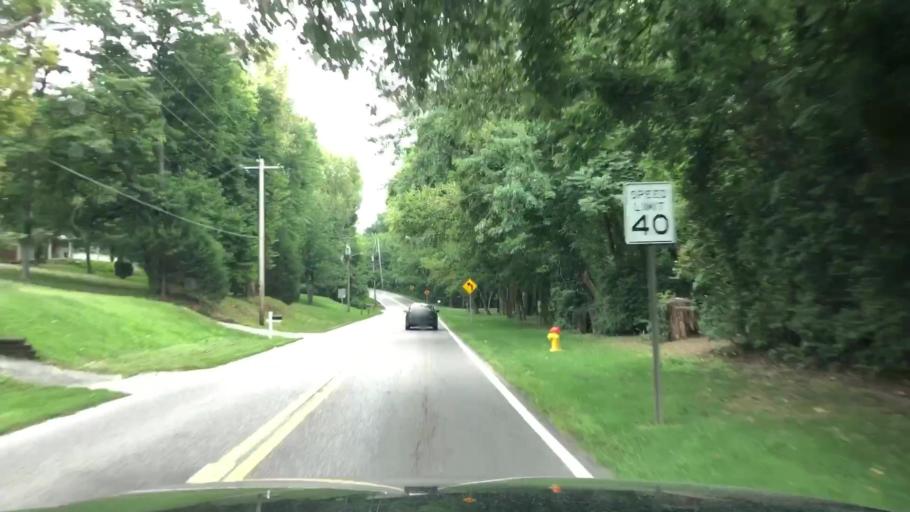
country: US
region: Missouri
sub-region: Saint Louis County
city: Hazelwood
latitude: 38.8097
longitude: -90.3849
